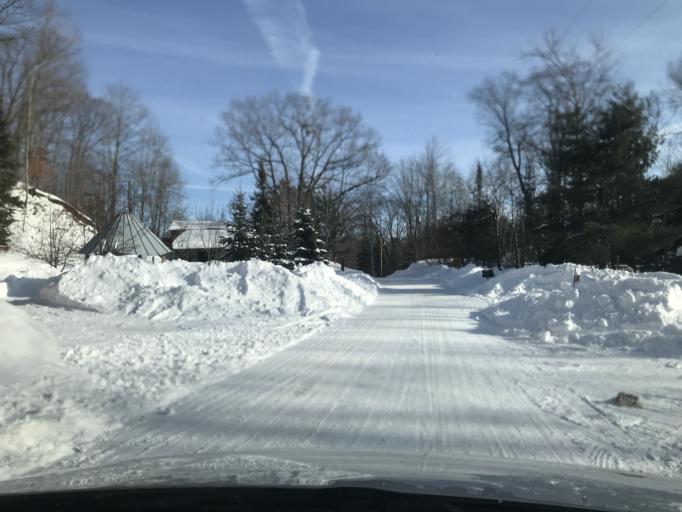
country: US
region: Wisconsin
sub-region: Menominee County
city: Legend Lake
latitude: 45.3432
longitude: -88.4540
